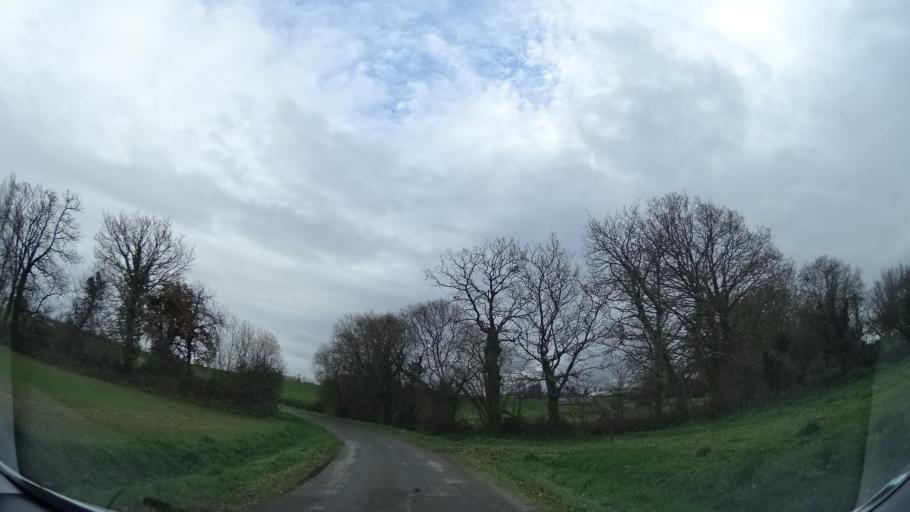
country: FR
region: Brittany
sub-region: Departement des Cotes-d'Armor
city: Evran
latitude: 48.3343
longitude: -1.9540
